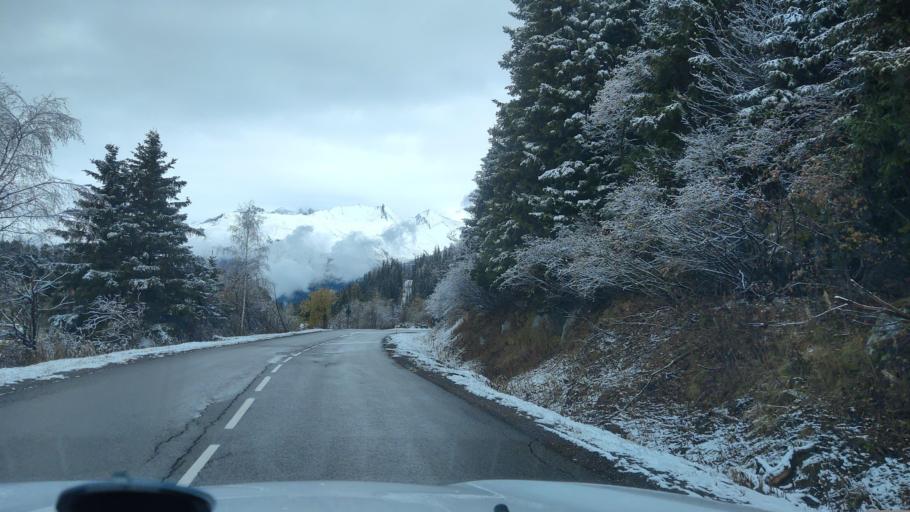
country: FR
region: Rhone-Alpes
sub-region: Departement de la Savoie
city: Seez
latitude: 45.5810
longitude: 6.8342
